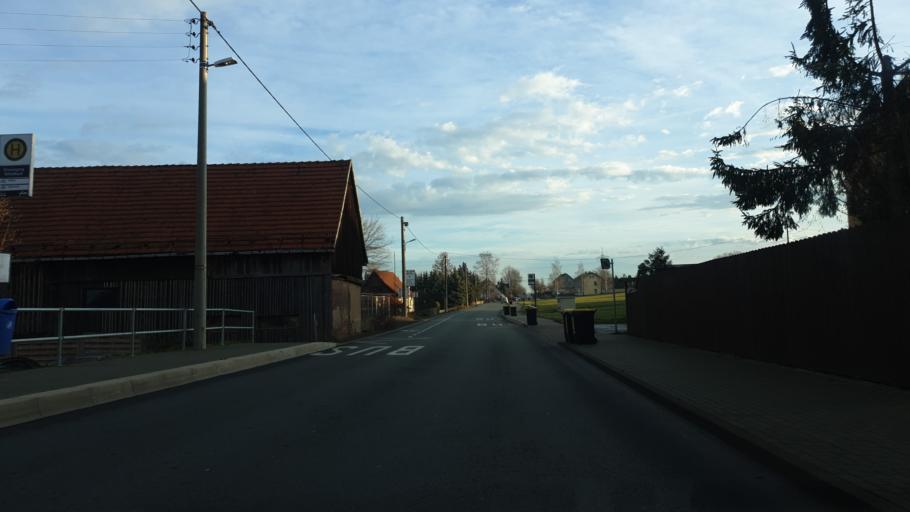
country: DE
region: Saxony
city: Neukirchen
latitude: 50.8059
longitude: 12.8080
